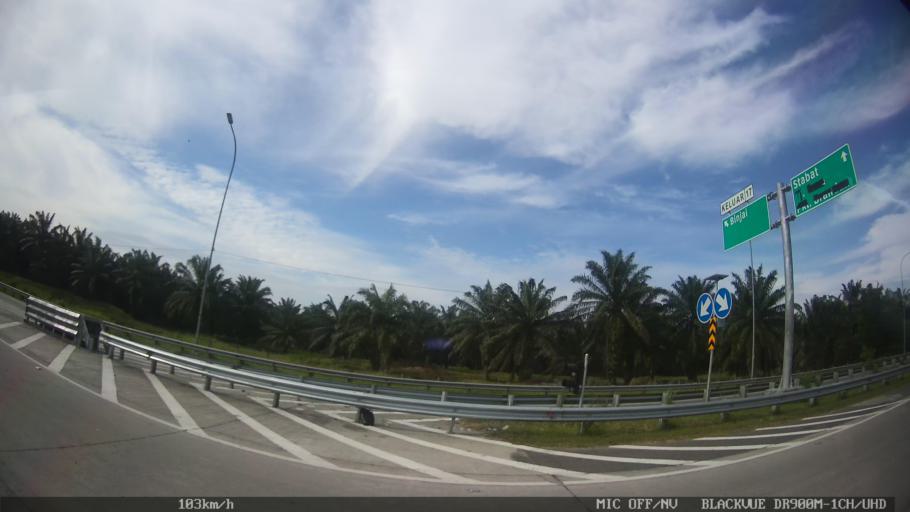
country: ID
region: North Sumatra
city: Binjai
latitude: 3.6468
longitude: 98.5490
